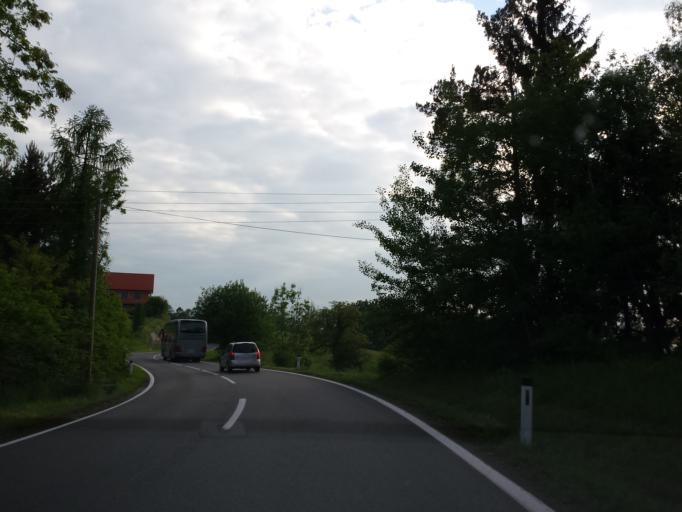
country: AT
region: Styria
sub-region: Graz Stadt
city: Mariatrost
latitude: 47.1029
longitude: 15.5390
